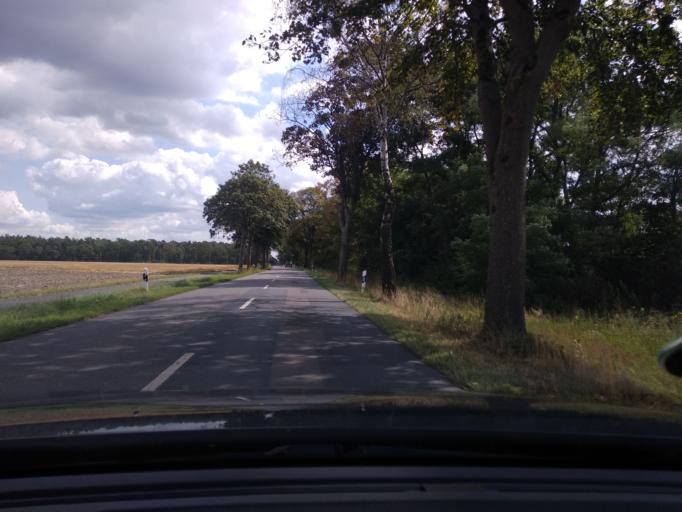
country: DE
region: Lower Saxony
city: Wagenhoff
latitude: 52.5097
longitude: 10.4937
